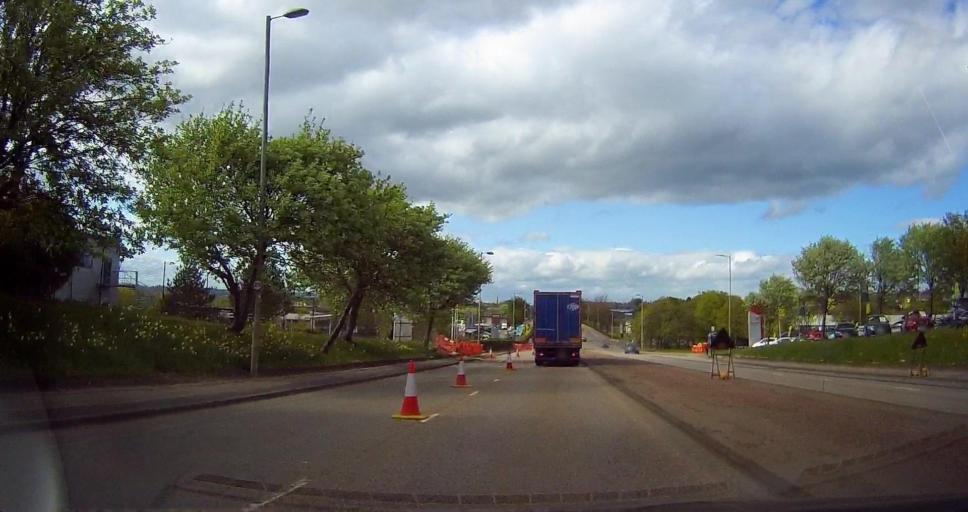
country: GB
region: Scotland
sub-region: Aberdeen City
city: Aberdeen
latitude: 57.1252
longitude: -2.0901
